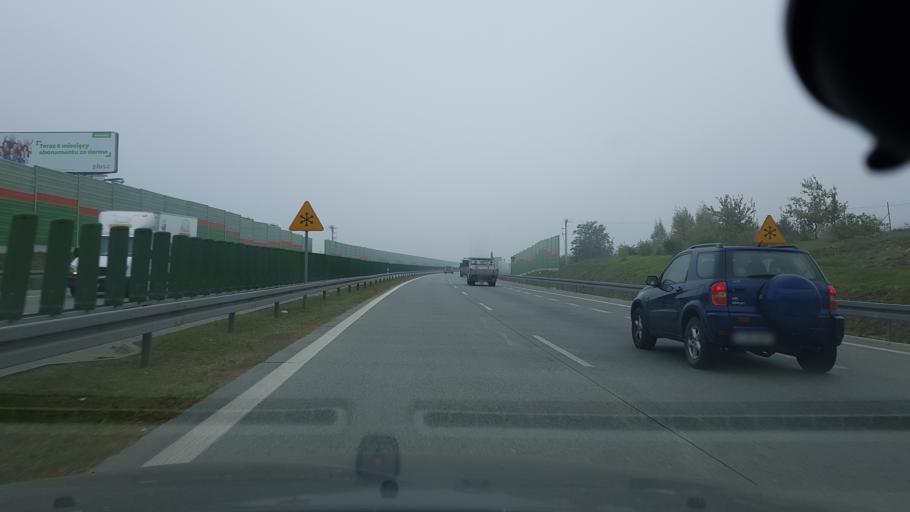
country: PL
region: Lodz Voivodeship
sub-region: Powiat rawski
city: Rawa Mazowiecka
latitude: 51.7694
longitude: 20.2727
